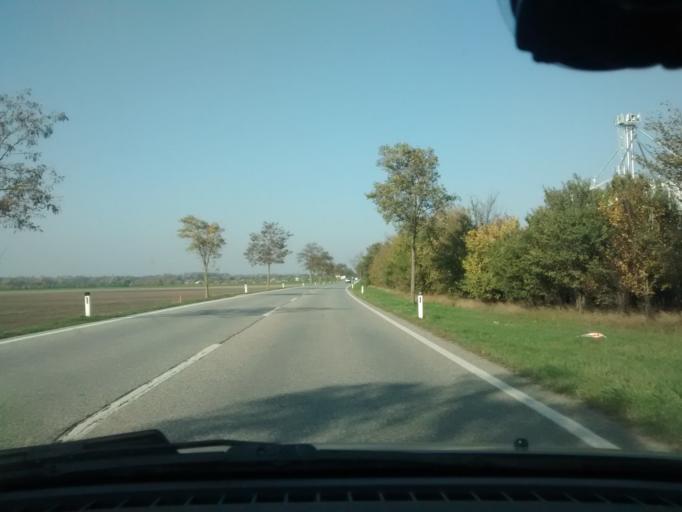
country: AT
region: Lower Austria
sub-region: Politischer Bezirk Modling
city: Munchendorf
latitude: 48.0489
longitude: 16.3820
